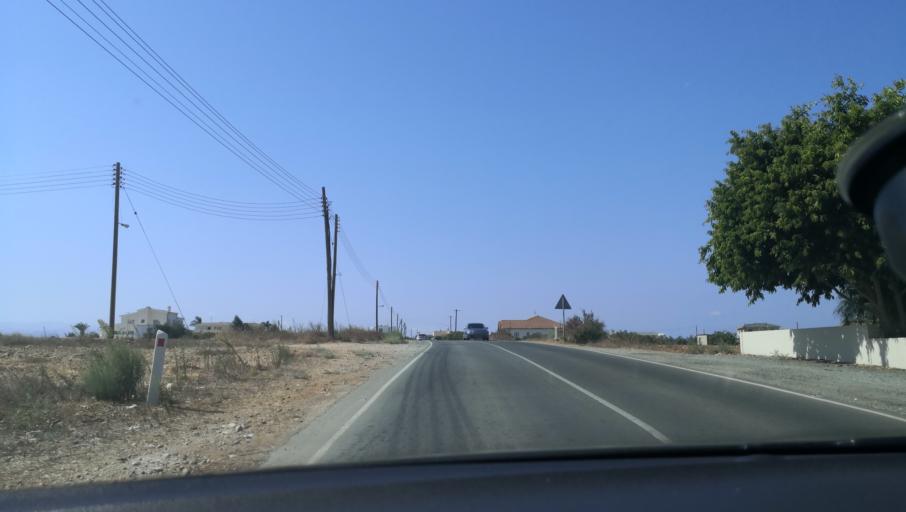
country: CY
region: Lefkosia
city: Kokkinotrimithia
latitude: 35.1158
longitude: 33.2250
